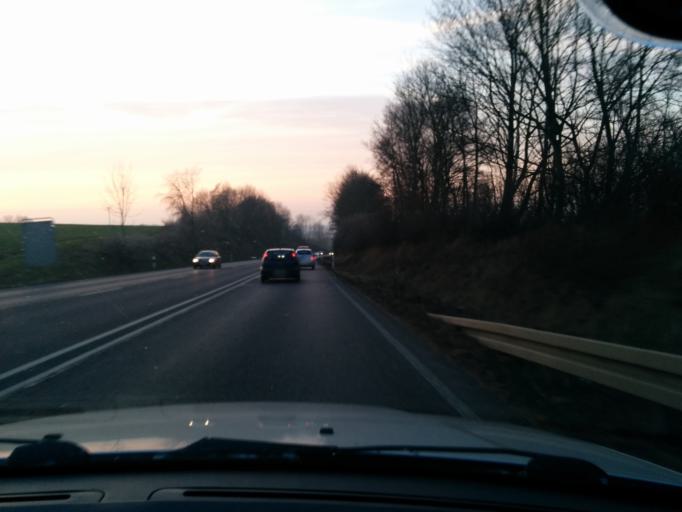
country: DE
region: Hesse
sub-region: Regierungsbezirk Kassel
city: Kaufungen
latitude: 51.2787
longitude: 9.6032
